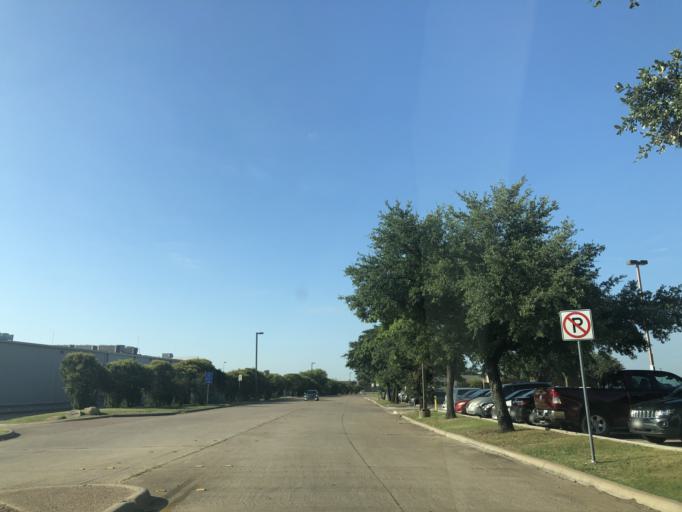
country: US
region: Texas
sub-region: Dallas County
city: Grand Prairie
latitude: 32.7410
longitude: -97.0178
